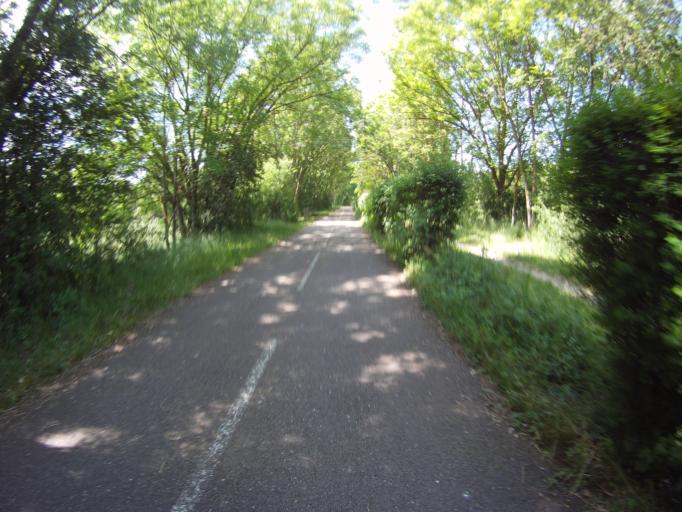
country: FR
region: Lorraine
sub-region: Departement de Meurthe-et-Moselle
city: Eulmont
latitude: 48.7432
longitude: 6.2164
